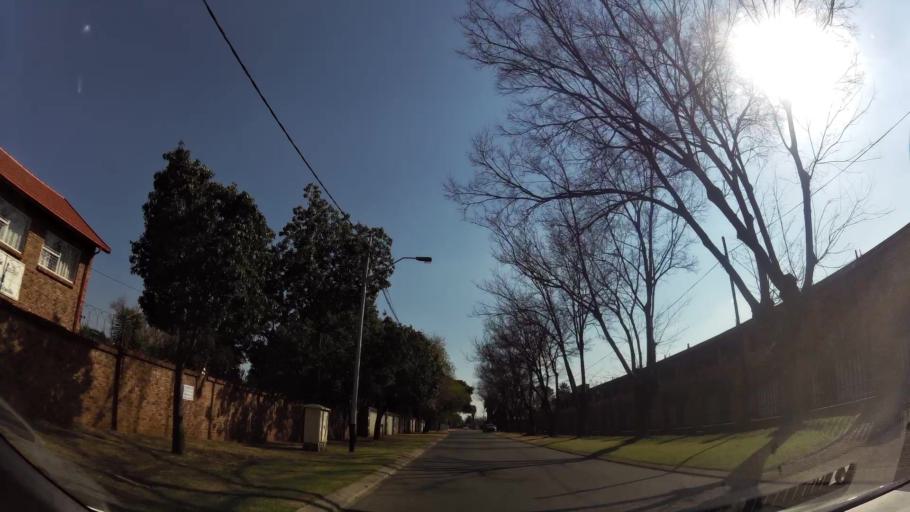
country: ZA
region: Gauteng
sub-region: Ekurhuleni Metropolitan Municipality
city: Boksburg
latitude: -26.1823
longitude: 28.2801
